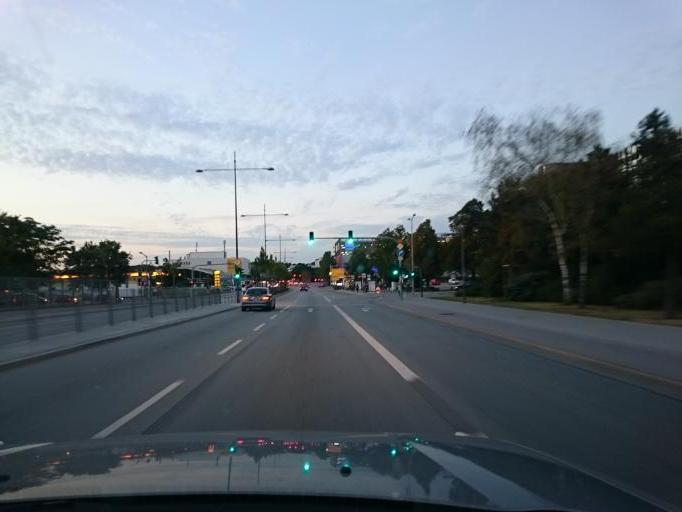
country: DE
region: Bavaria
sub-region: Upper Palatinate
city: Regensburg
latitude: 49.0246
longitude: 12.1138
